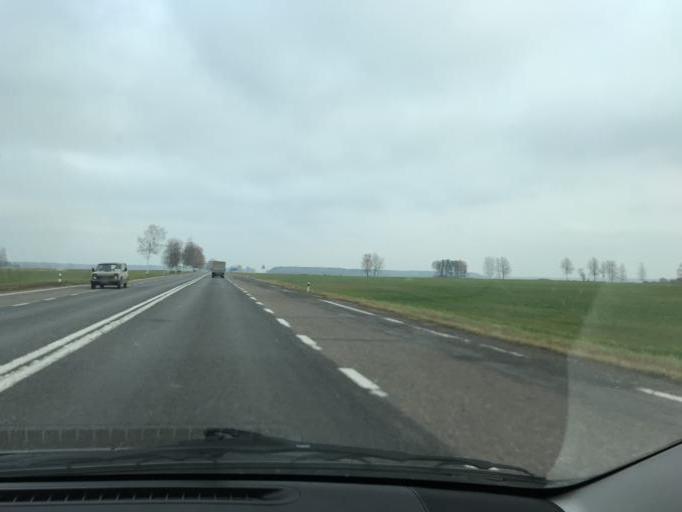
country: BY
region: Vitebsk
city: Syanno
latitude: 55.0818
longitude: 29.5862
